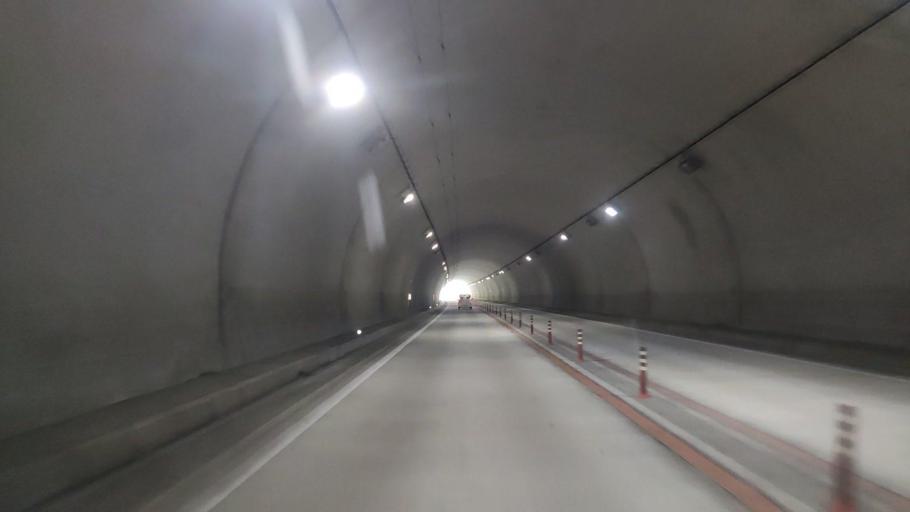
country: JP
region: Wakayama
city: Shingu
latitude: 33.6158
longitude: 135.9172
